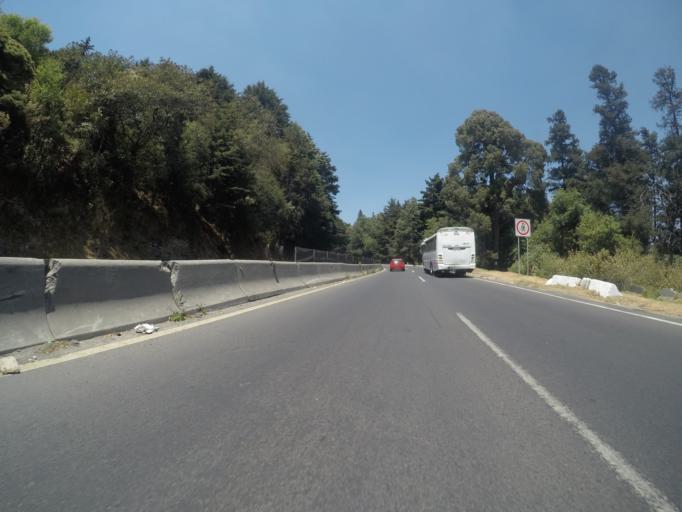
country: MX
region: Mexico City
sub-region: Cuajimalpa de Morelos
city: San Lorenzo Acopilco
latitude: 19.3151
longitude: -99.3281
